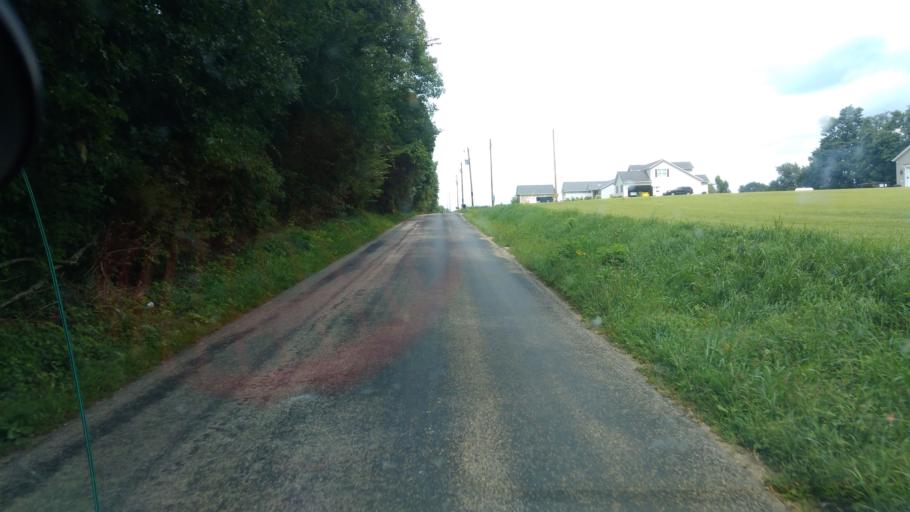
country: US
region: Ohio
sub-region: Ashland County
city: Ashland
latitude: 40.7932
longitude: -82.3592
